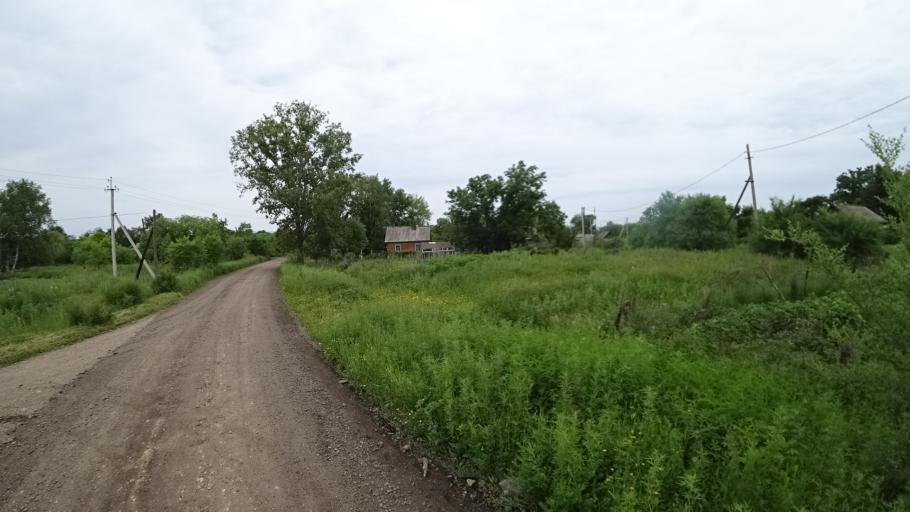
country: RU
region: Primorskiy
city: Novosysoyevka
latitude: 44.2101
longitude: 133.3396
